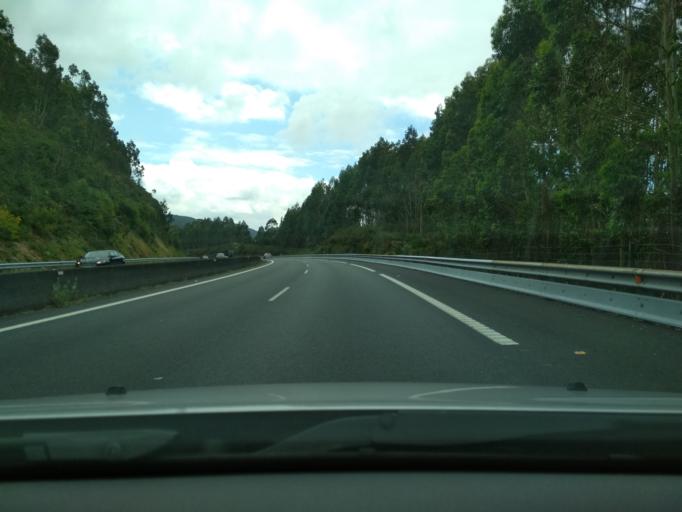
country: ES
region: Galicia
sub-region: Provincia da Coruna
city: Padron
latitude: 42.7839
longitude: -8.6445
